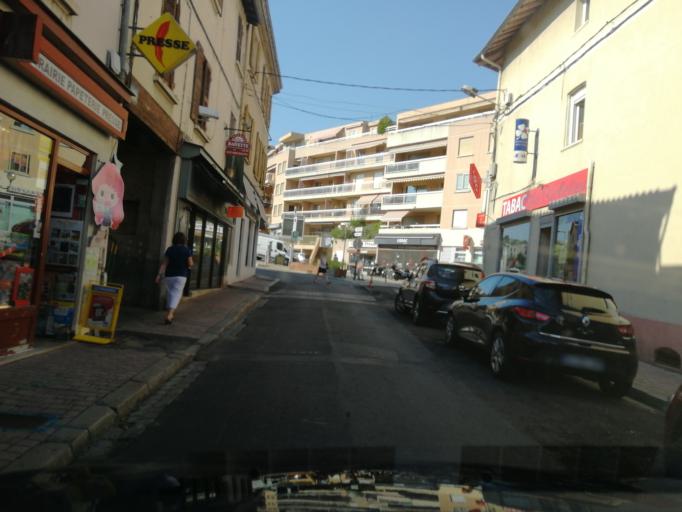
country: FR
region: Rhone-Alpes
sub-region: Departement du Rhone
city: Fontaines-sur-Saone
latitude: 45.8345
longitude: 4.8476
